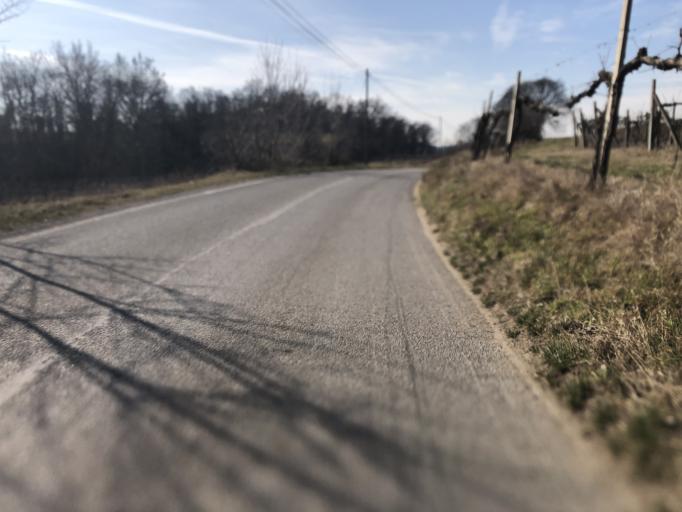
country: IT
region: Veneto
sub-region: Provincia di Verona
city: San Giorgio in Salici
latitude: 45.3974
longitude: 10.7717
